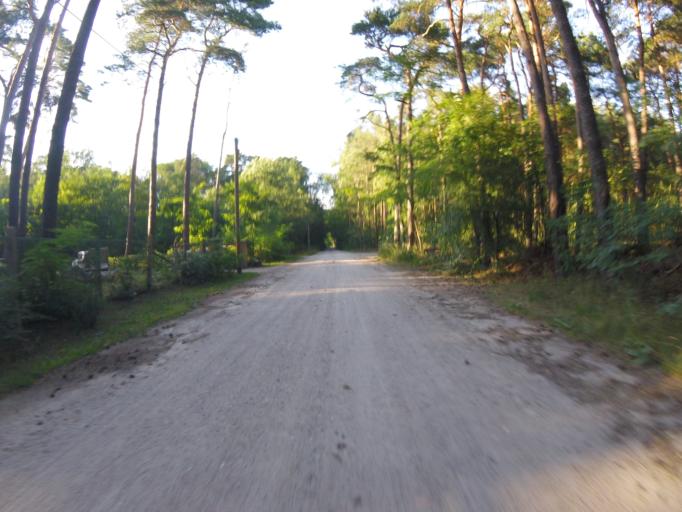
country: DE
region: Brandenburg
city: Gross Koris
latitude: 52.1829
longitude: 13.6563
